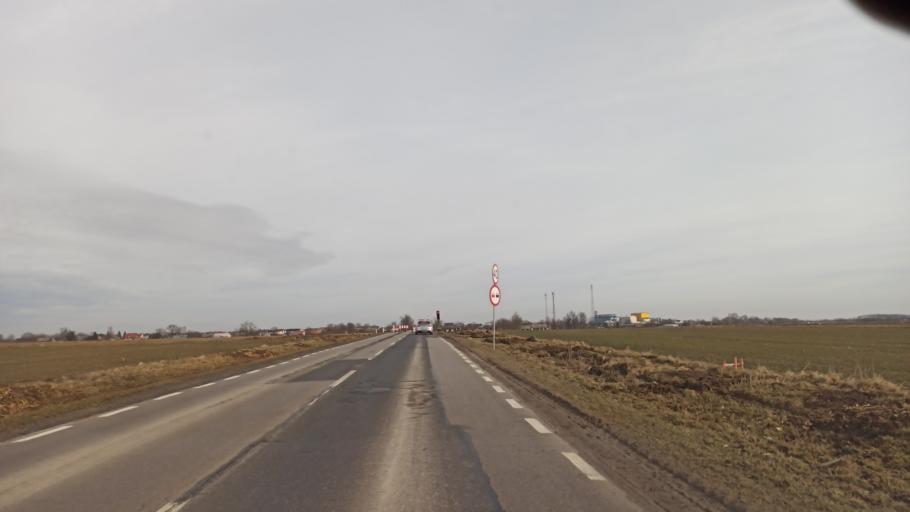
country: PL
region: Lublin Voivodeship
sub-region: Powiat bilgorajski
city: Tarnogrod
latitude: 50.3424
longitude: 22.7329
